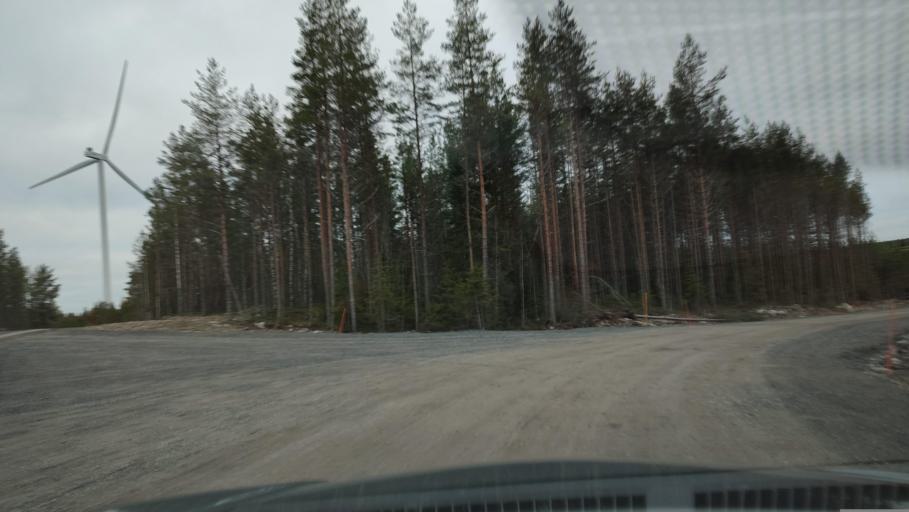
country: FI
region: Southern Ostrobothnia
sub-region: Suupohja
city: Karijoki
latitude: 62.1992
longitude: 21.5900
